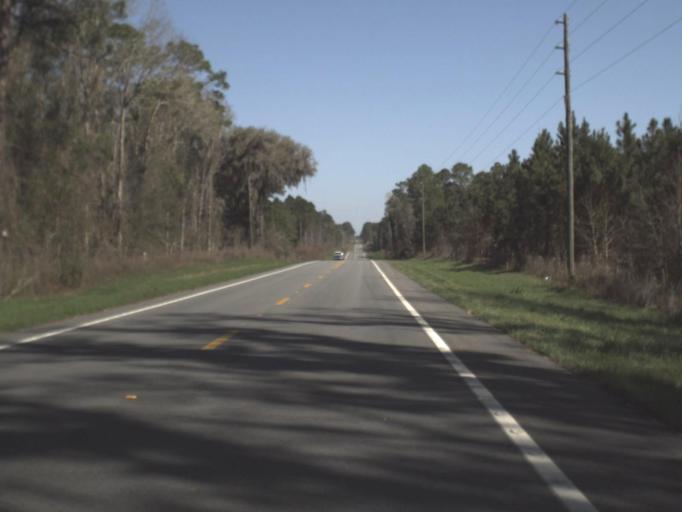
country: US
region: Florida
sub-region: Jefferson County
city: Monticello
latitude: 30.4185
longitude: -84.0203
